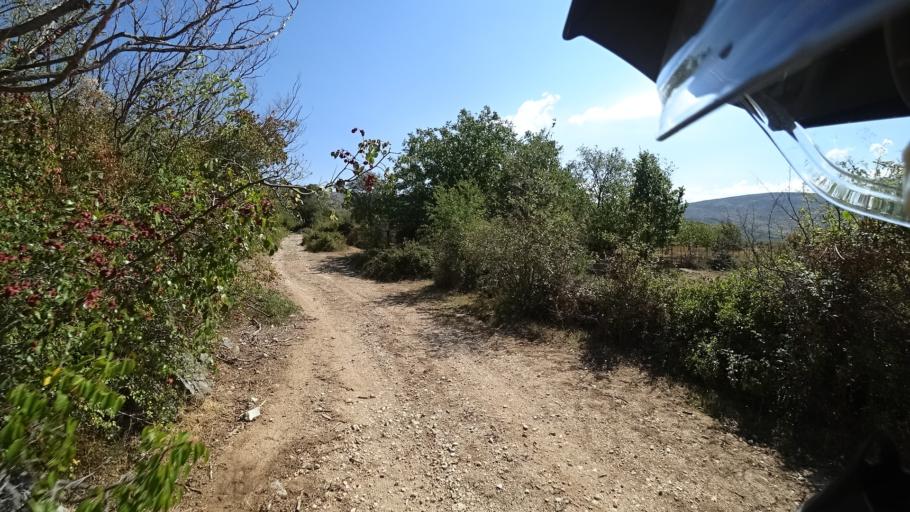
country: HR
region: Sibensko-Kniniska
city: Drnis
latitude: 43.8131
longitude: 16.3345
